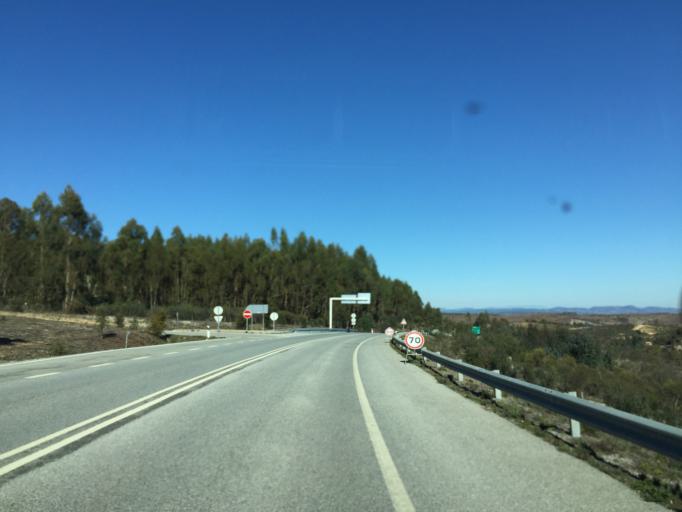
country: PT
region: Portalegre
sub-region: Nisa
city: Nisa
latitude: 39.4986
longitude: -7.7684
